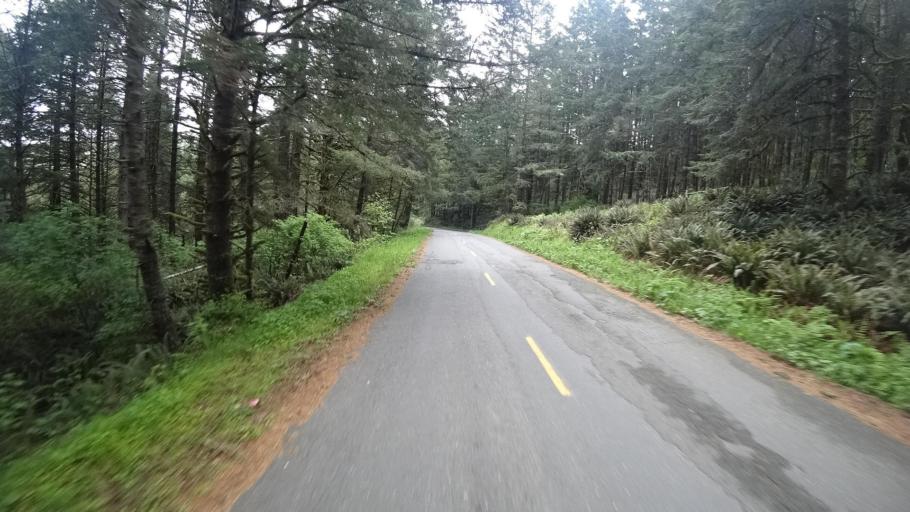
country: US
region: California
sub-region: Humboldt County
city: Ferndale
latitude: 40.4946
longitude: -124.3120
